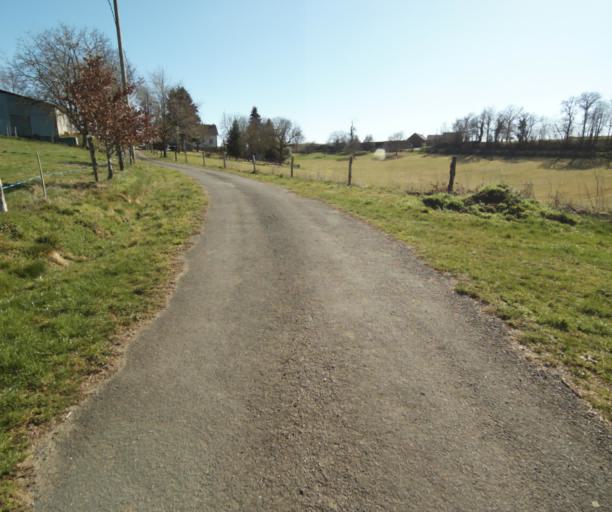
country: FR
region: Limousin
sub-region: Departement de la Correze
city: Chamboulive
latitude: 45.4218
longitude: 1.6667
